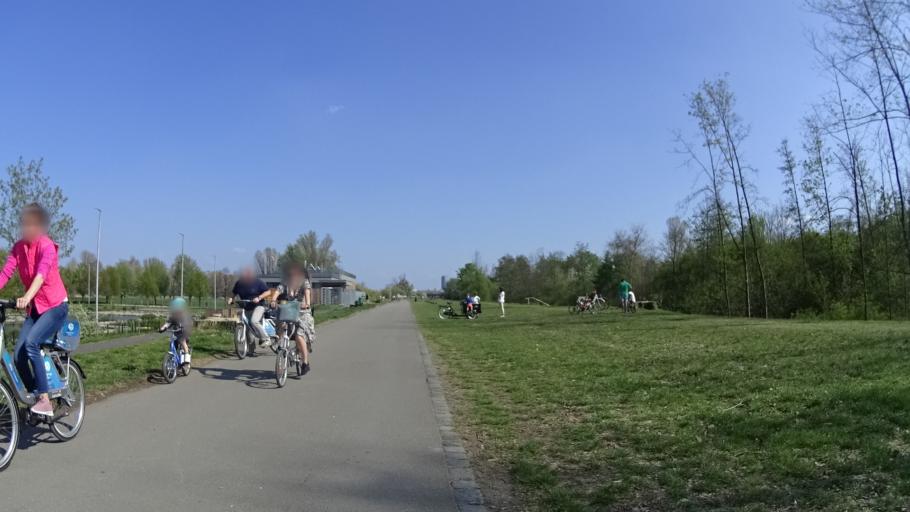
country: DE
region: North Rhine-Westphalia
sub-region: Regierungsbezirk Dusseldorf
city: Dusseldorf
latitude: 51.2485
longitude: 6.7394
